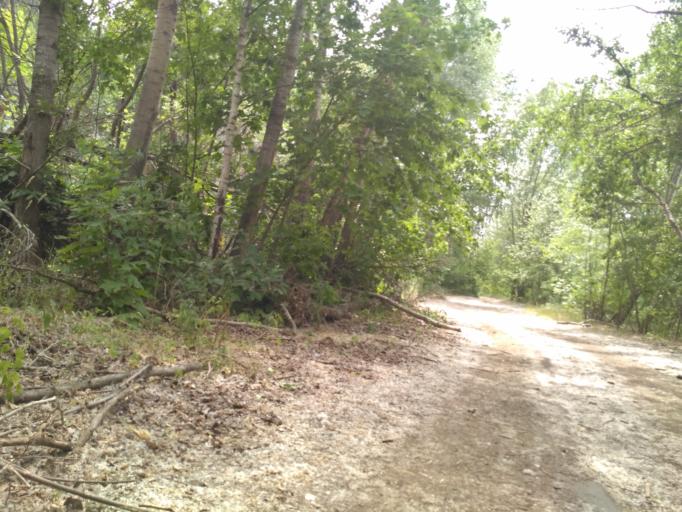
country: RU
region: Nizjnij Novgorod
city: Nizhniy Novgorod
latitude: 56.3053
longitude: 43.9684
